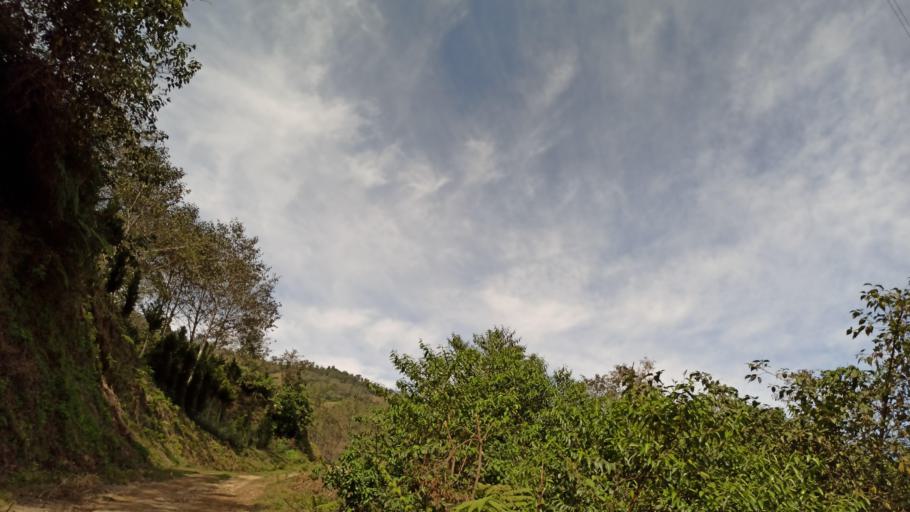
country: MX
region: Veracruz
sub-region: La Perla
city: Metlac Hernandez (Metlac Primero)
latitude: 18.9729
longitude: -97.1044
